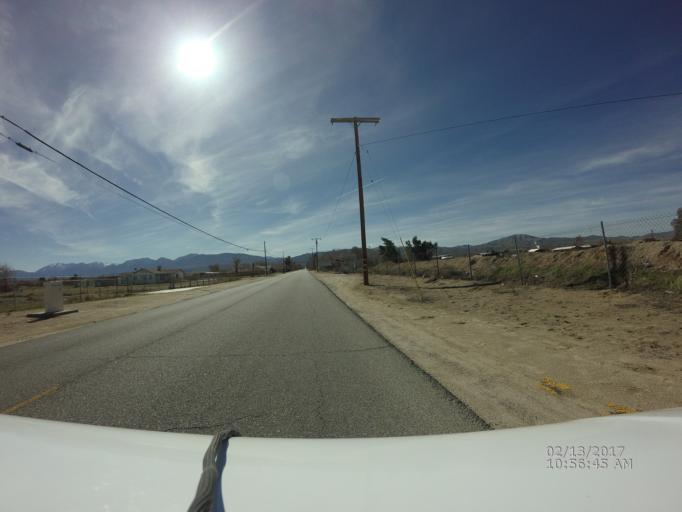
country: US
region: California
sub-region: Los Angeles County
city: Littlerock
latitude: 34.5422
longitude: -117.9838
